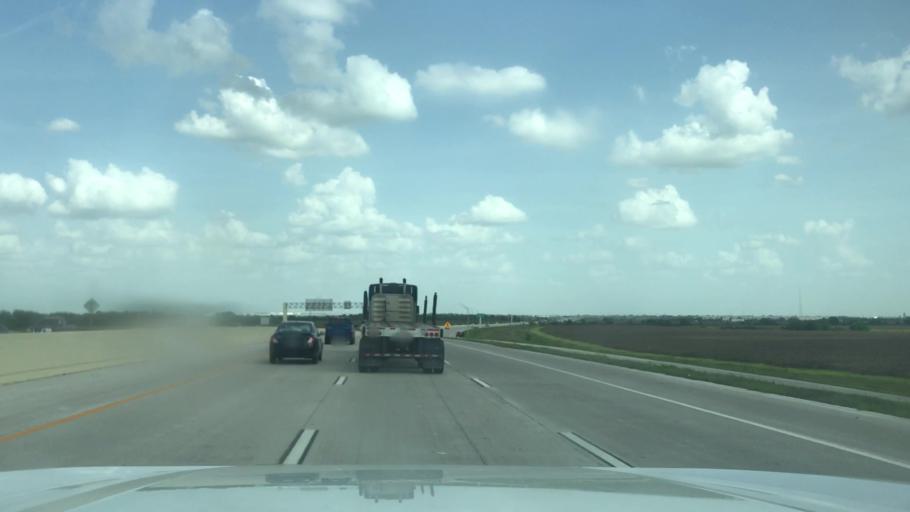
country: US
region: Texas
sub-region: Waller County
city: Waller
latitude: 30.0572
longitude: -95.8904
